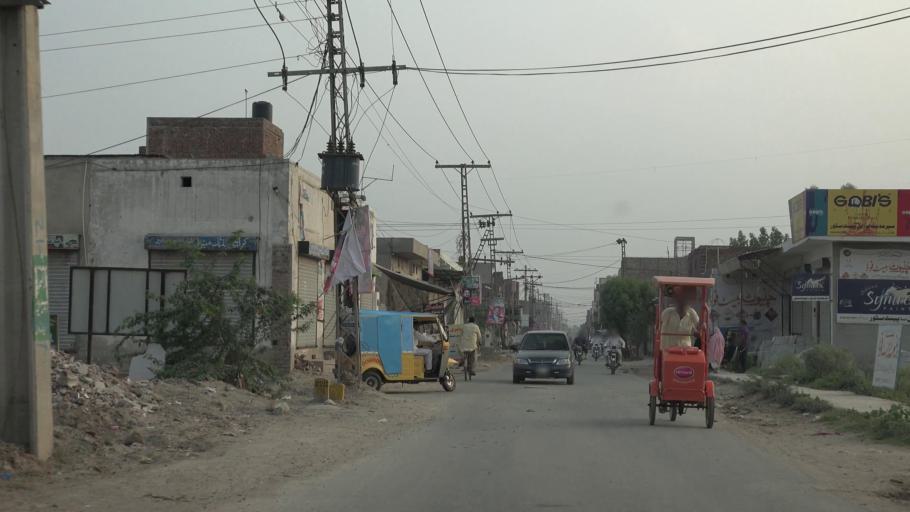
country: PK
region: Punjab
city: Faisalabad
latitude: 31.4319
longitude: 73.1422
